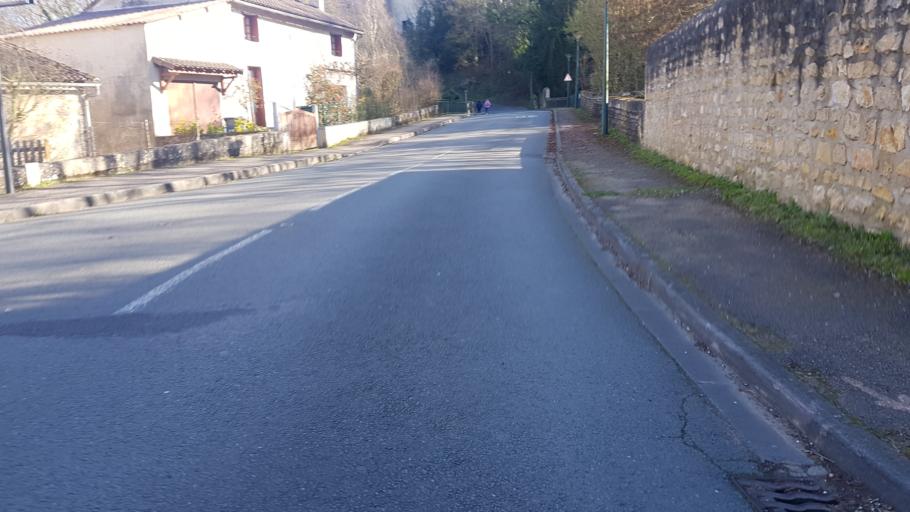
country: FR
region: Poitou-Charentes
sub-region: Departement de la Vienne
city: Migne-Auxances
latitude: 46.6249
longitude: 0.3139
